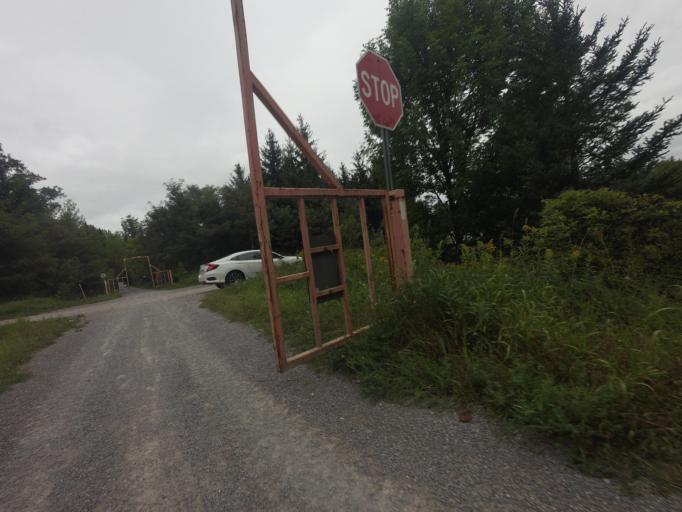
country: CA
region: Ontario
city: Omemee
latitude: 44.4057
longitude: -78.7662
